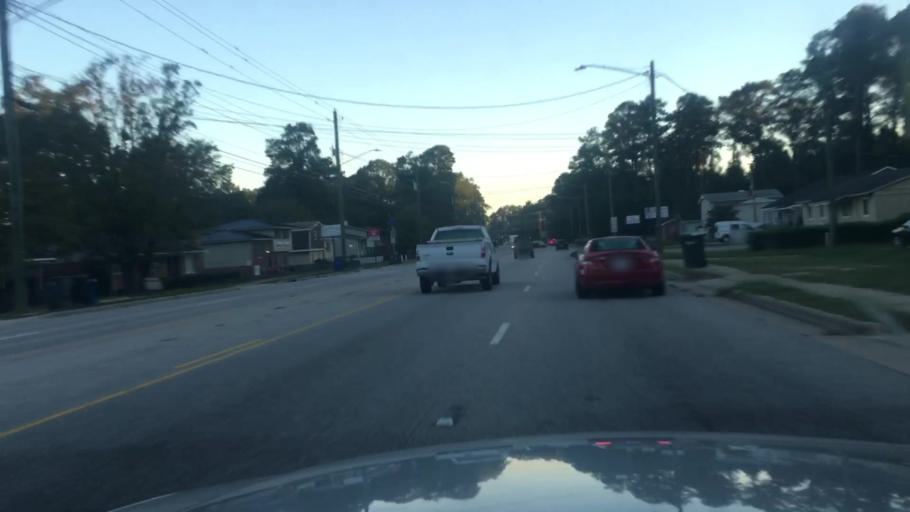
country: US
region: North Carolina
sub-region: Cumberland County
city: Hope Mills
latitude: 35.0199
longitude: -78.9626
